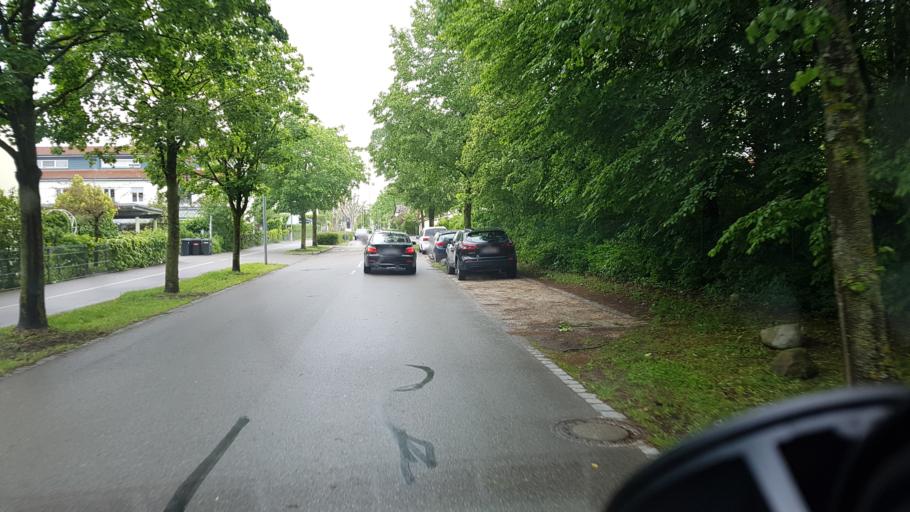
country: DE
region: Bavaria
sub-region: Upper Bavaria
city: Burghausen
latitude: 48.1650
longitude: 12.8142
